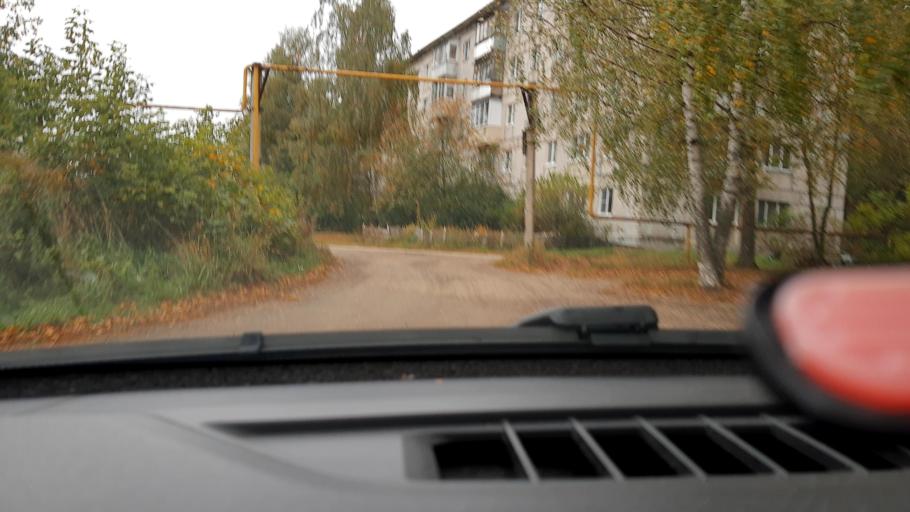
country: RU
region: Nizjnij Novgorod
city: Burevestnik
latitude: 56.1622
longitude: 43.9224
